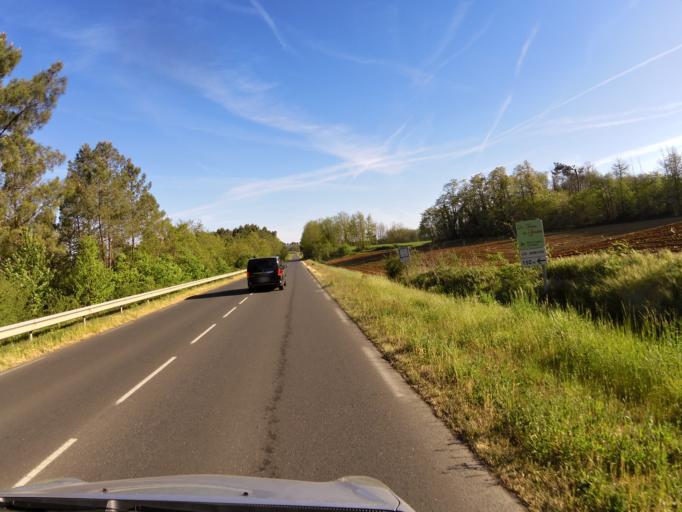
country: FR
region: Aquitaine
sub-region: Departement de la Dordogne
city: Sarlat-la-Caneda
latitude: 44.9675
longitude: 1.2375
